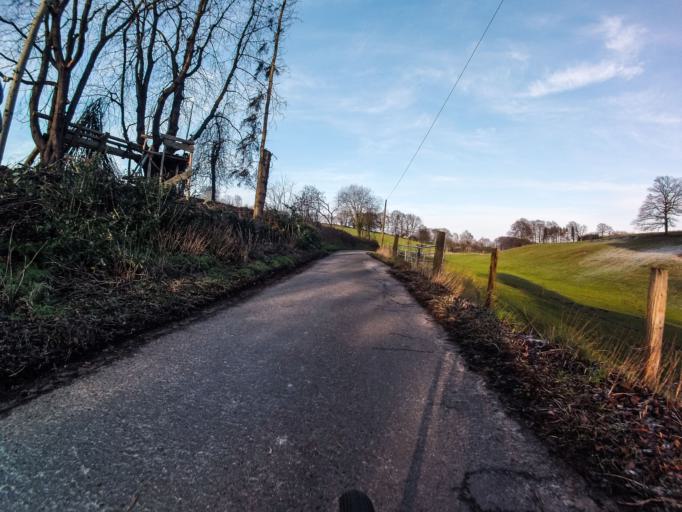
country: DE
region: North Rhine-Westphalia
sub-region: Regierungsbezirk Munster
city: Mettingen
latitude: 52.2752
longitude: 7.7985
